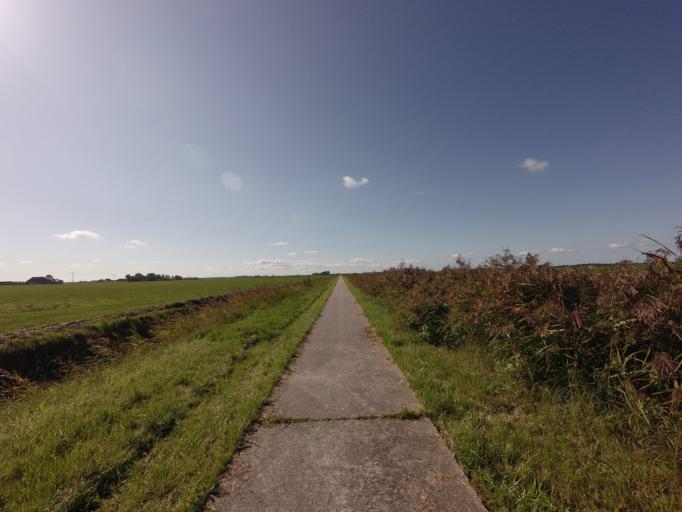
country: NL
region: Friesland
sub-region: Gemeente Boarnsterhim
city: Reduzum
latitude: 53.1388
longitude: 5.7617
